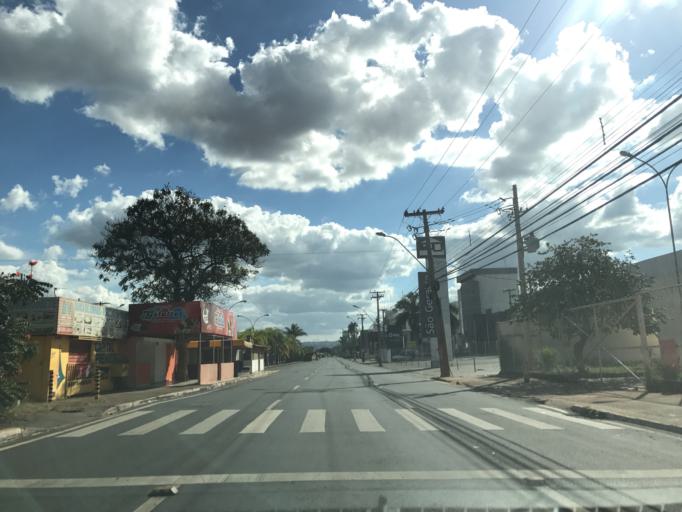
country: BR
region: Federal District
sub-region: Brasilia
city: Brasilia
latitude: -15.8041
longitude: -47.9579
